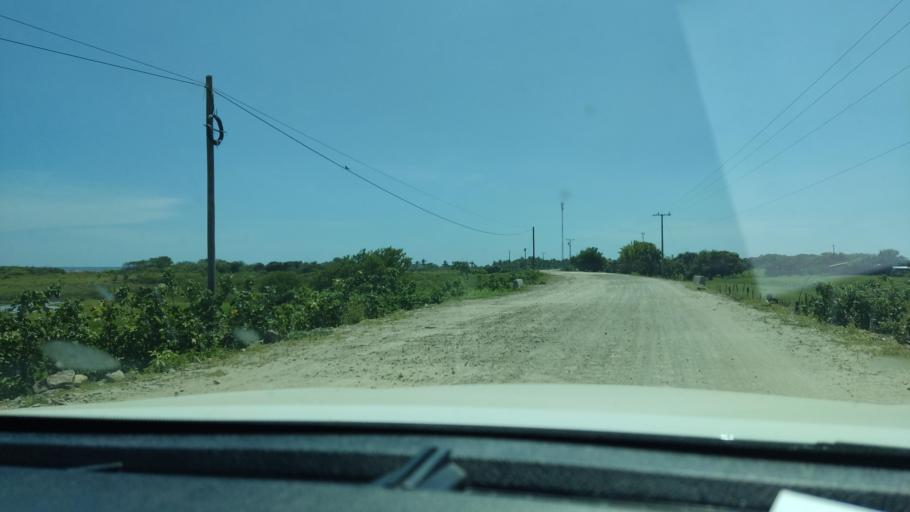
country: SV
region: Ahuachapan
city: San Francisco Menendez
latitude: 13.7658
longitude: -90.1718
